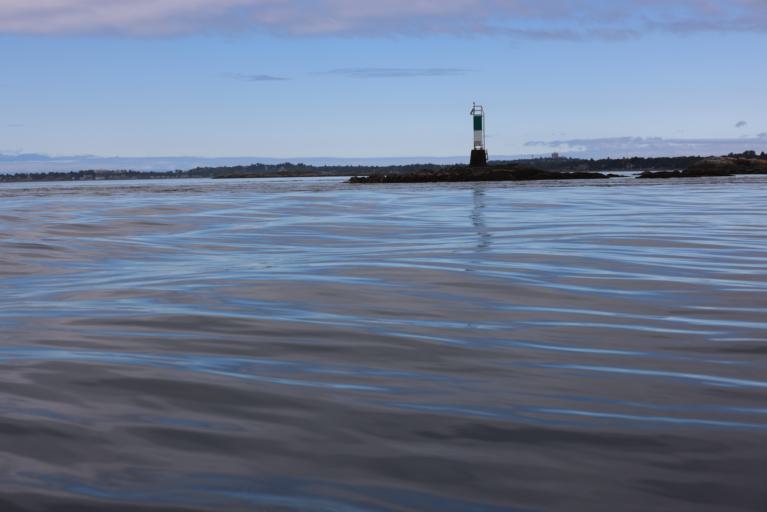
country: CA
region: British Columbia
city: Oak Bay
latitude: 48.4510
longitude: -123.2624
